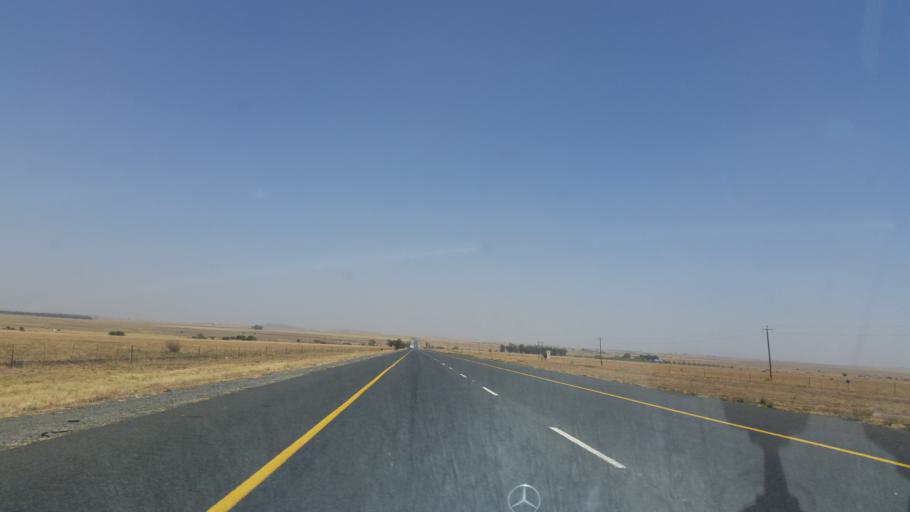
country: ZA
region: Orange Free State
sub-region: Lejweleputswa District Municipality
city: Winburg
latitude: -28.7208
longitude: 26.7715
